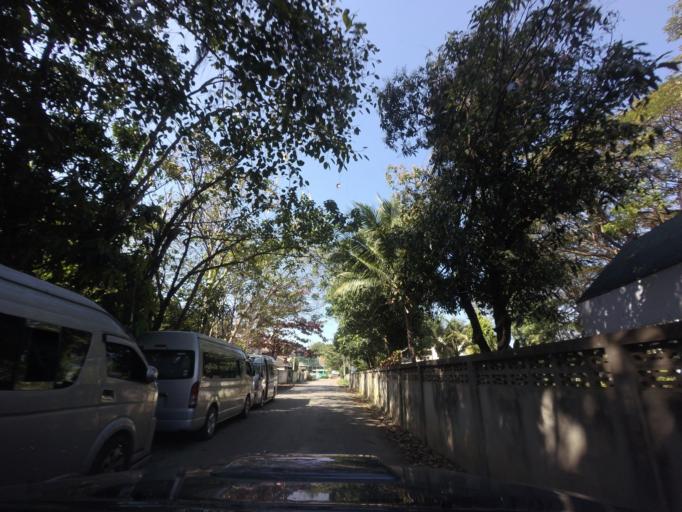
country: TH
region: Chiang Mai
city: Chiang Mai
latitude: 18.7684
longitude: 99.0040
